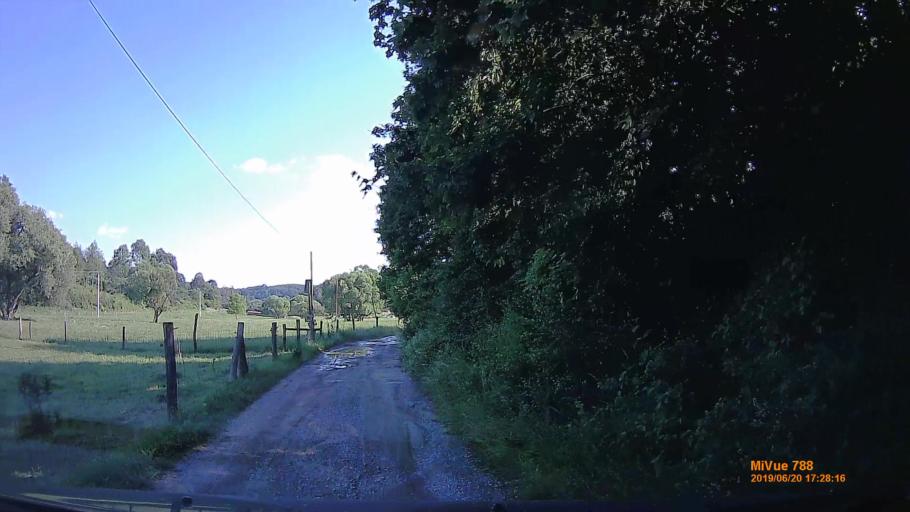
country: HU
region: Baranya
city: Buekkoesd
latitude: 46.1588
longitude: 18.0108
